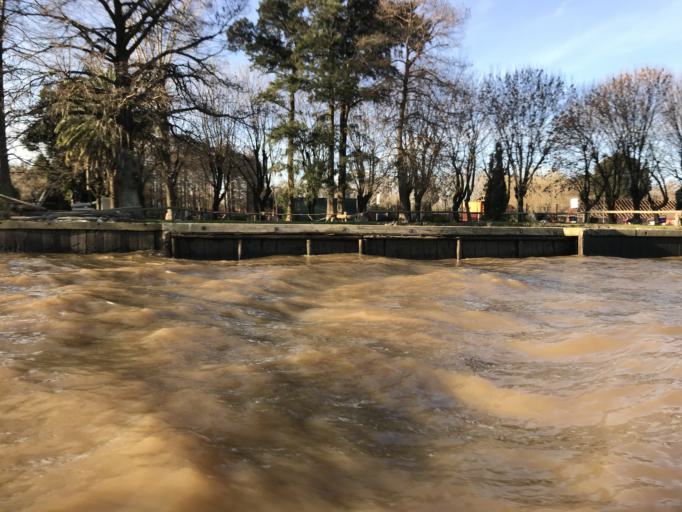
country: AR
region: Buenos Aires
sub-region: Partido de Tigre
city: Tigre
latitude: -34.4085
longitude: -58.5900
